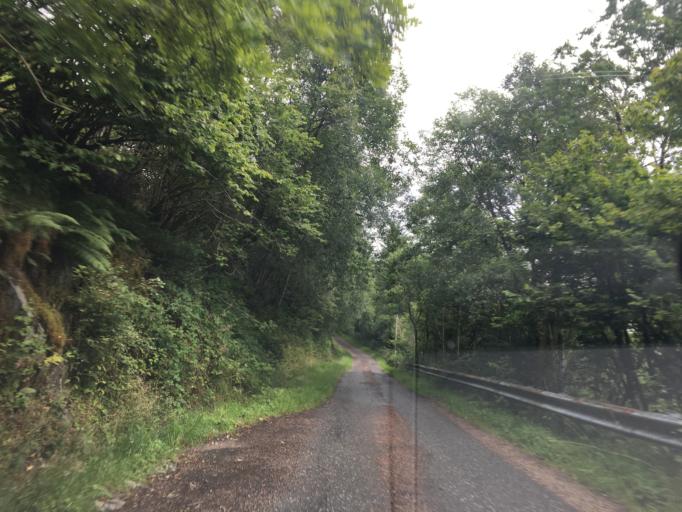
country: GB
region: Scotland
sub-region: Argyll and Bute
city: Oban
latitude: 56.2691
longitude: -5.3731
